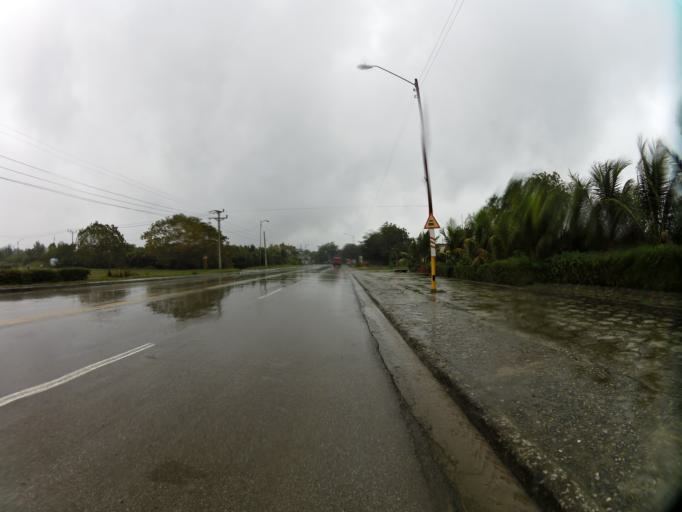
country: CU
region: Las Tunas
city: Las Tunas
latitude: 20.9627
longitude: -76.9409
